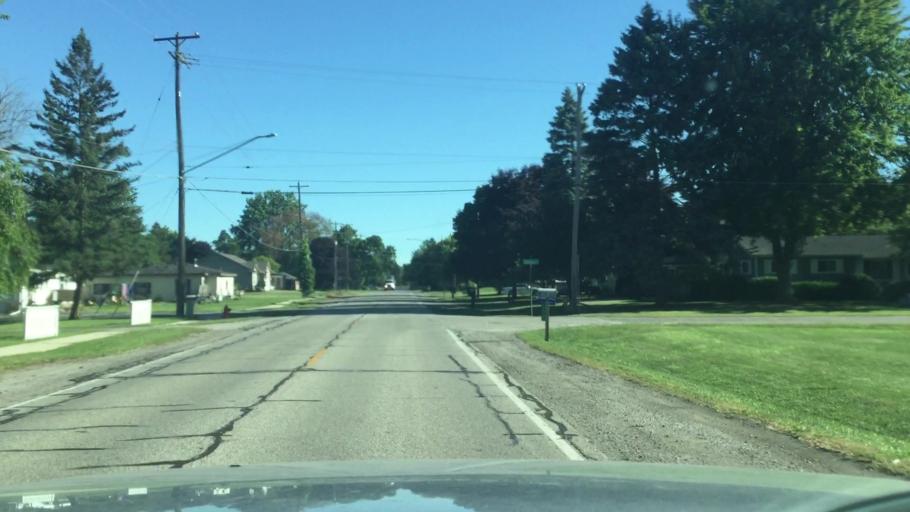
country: US
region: Michigan
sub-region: Saginaw County
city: Shields
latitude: 43.4182
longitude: -84.0520
